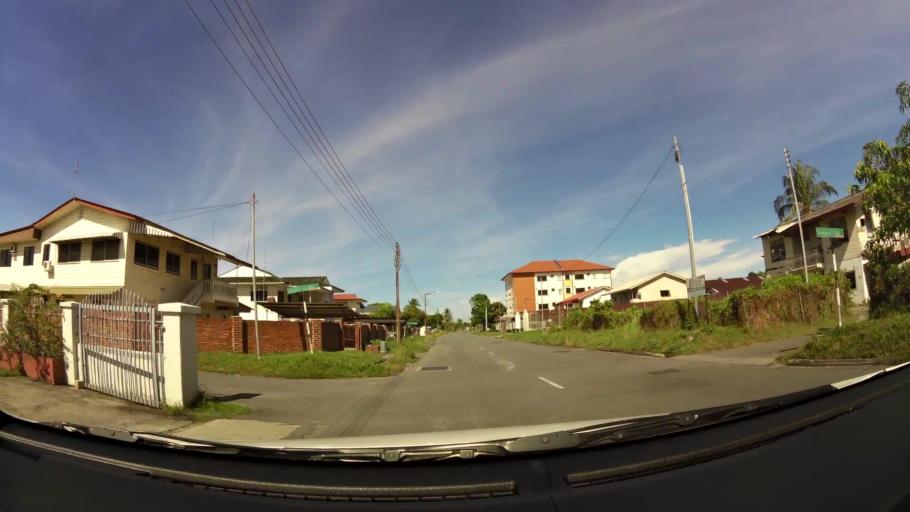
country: BN
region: Belait
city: Kuala Belait
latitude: 4.5862
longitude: 114.2079
